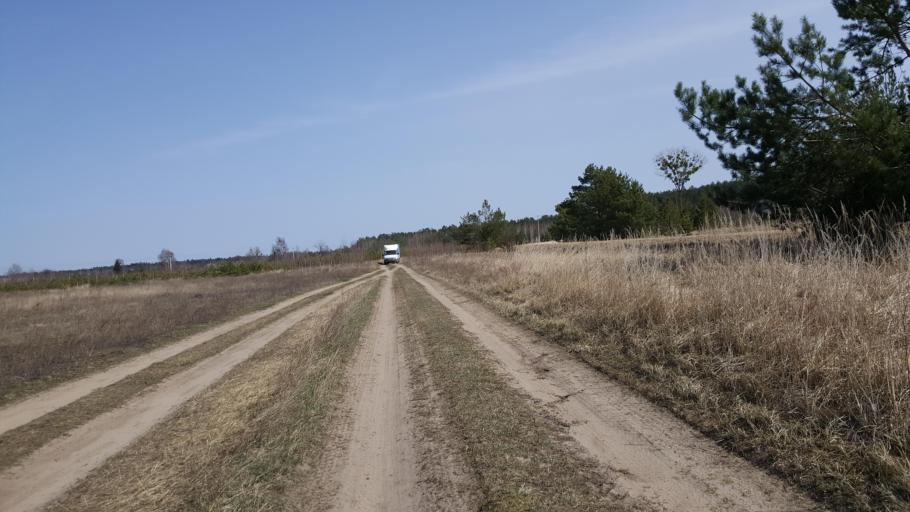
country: BY
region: Brest
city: Kamyanyuki
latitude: 52.5635
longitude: 23.7681
